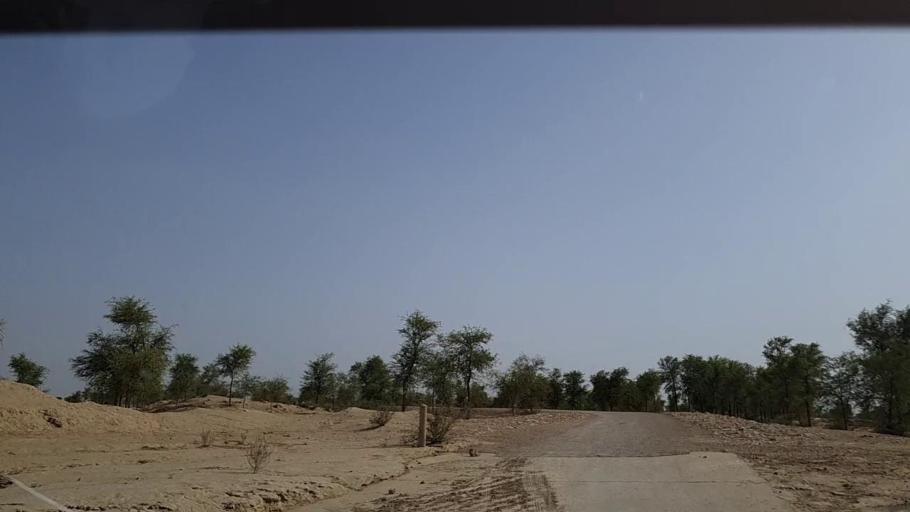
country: PK
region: Sindh
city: Johi
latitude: 26.6112
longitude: 67.4942
